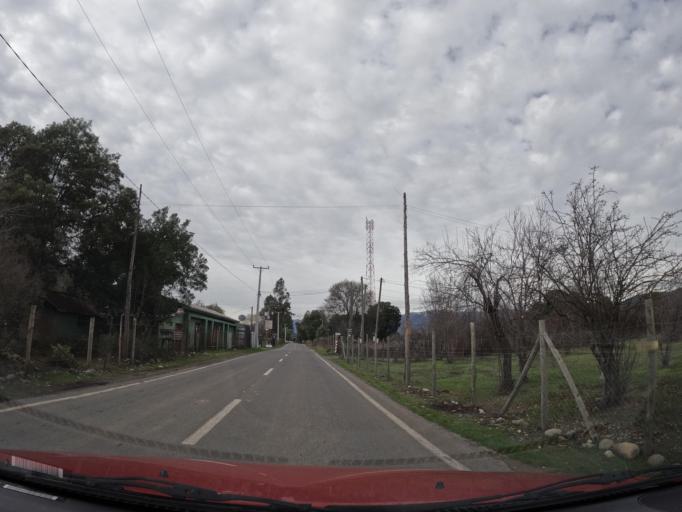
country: CL
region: Maule
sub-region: Provincia de Linares
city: Linares
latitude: -35.9236
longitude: -71.4097
